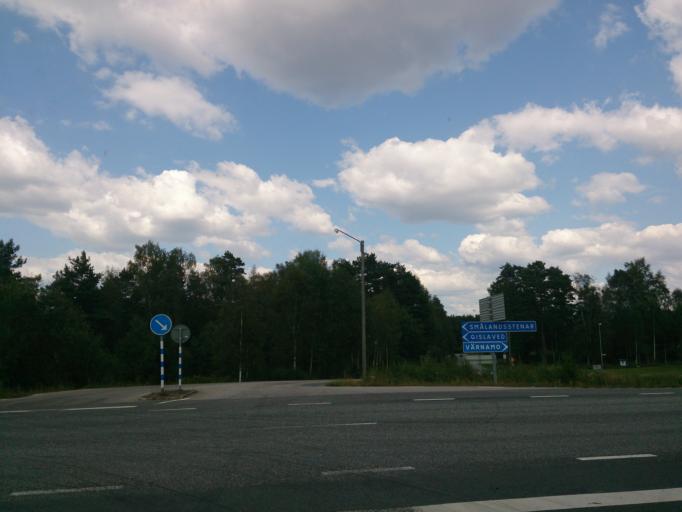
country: SE
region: Joenkoeping
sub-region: Varnamo Kommun
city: Forsheda
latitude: 57.1665
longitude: 13.8354
